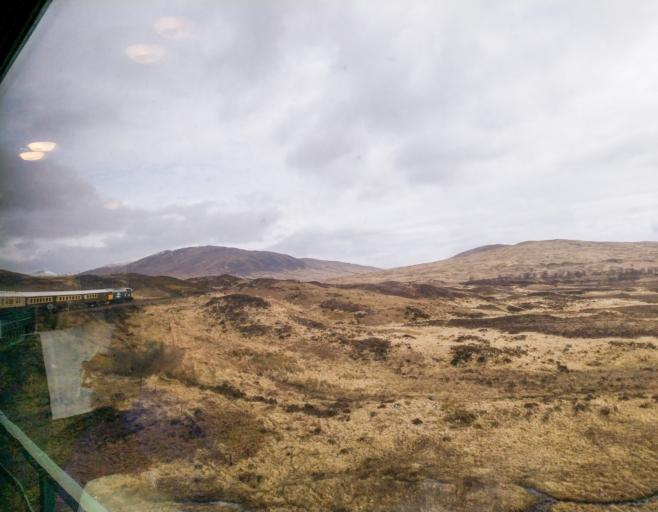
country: GB
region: Scotland
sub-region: Highland
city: Spean Bridge
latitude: 56.6901
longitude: -4.5769
